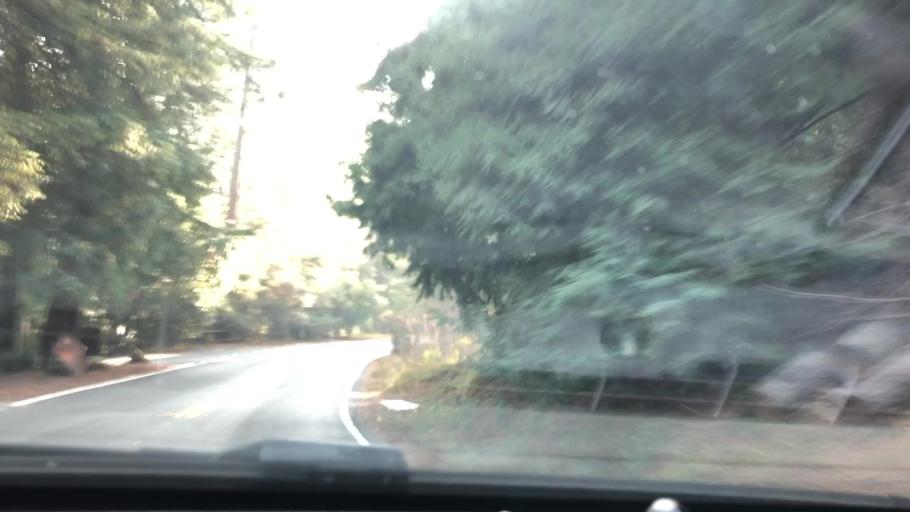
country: US
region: California
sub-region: Alameda County
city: Berkeley
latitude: 37.8873
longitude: -122.2449
